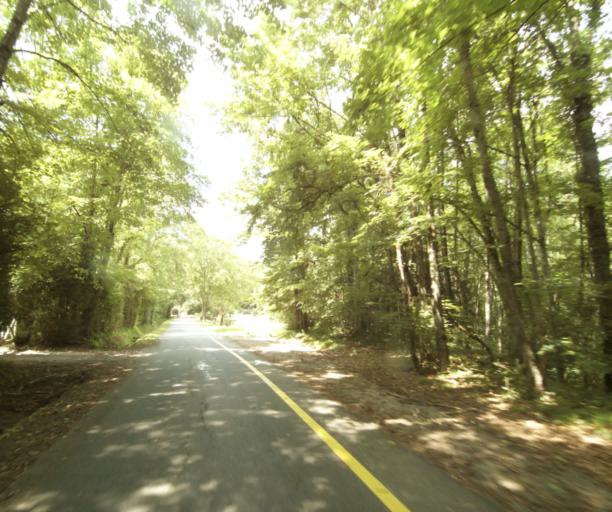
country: FR
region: Rhone-Alpes
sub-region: Departement de la Haute-Savoie
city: Chens-sur-Leman
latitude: 46.3231
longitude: 6.2612
